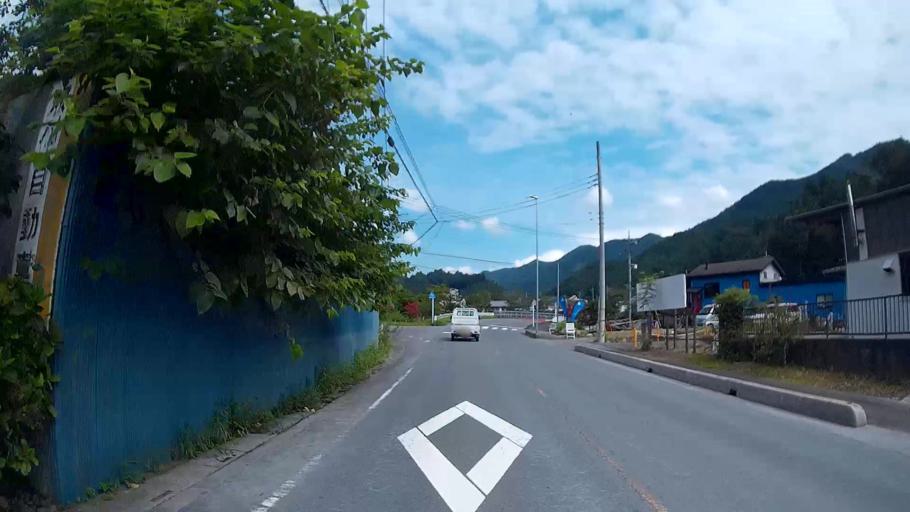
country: JP
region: Tokyo
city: Ome
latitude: 35.8650
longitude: 139.1869
